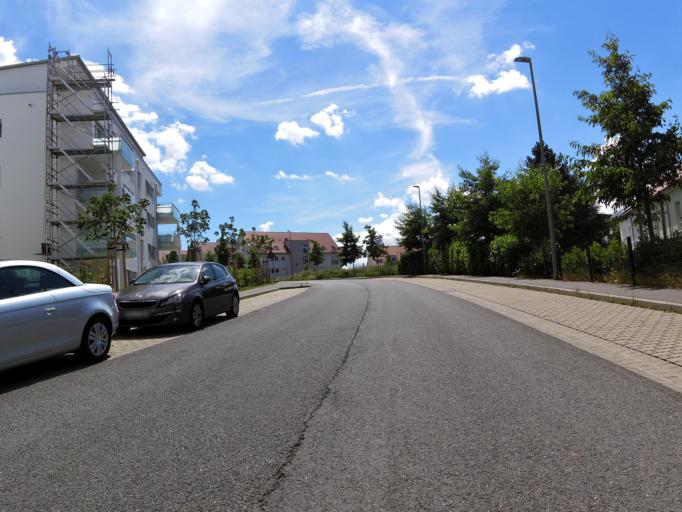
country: DE
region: Bavaria
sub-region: Regierungsbezirk Unterfranken
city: Estenfeld
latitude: 49.8059
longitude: 9.9902
